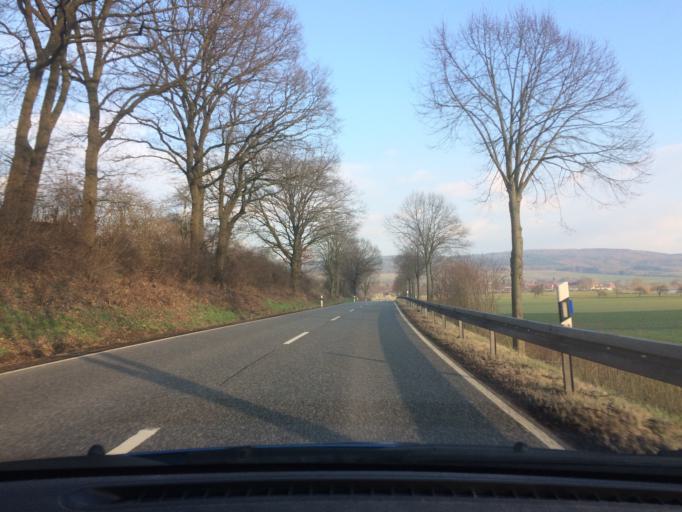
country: DE
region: Lower Saxony
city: Bodenfelde
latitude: 51.5992
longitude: 9.5798
